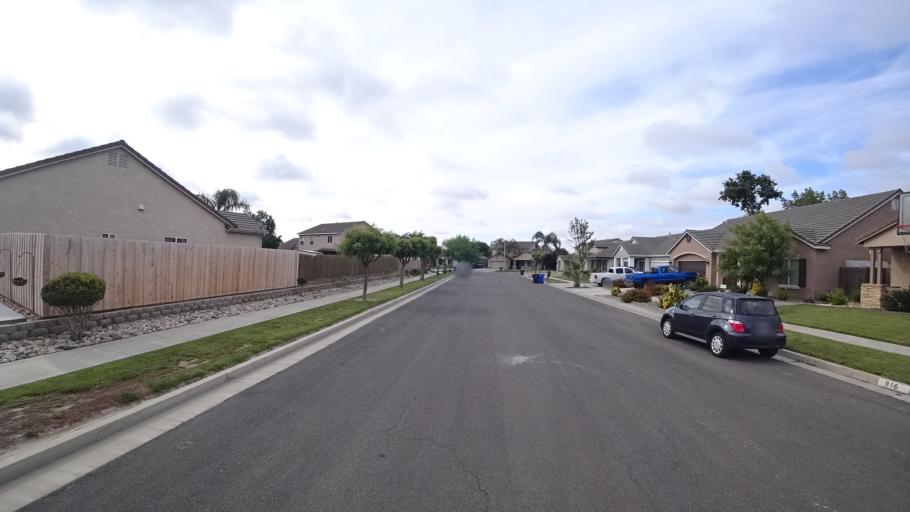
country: US
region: California
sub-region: Kings County
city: Hanford
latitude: 36.3340
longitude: -119.6788
